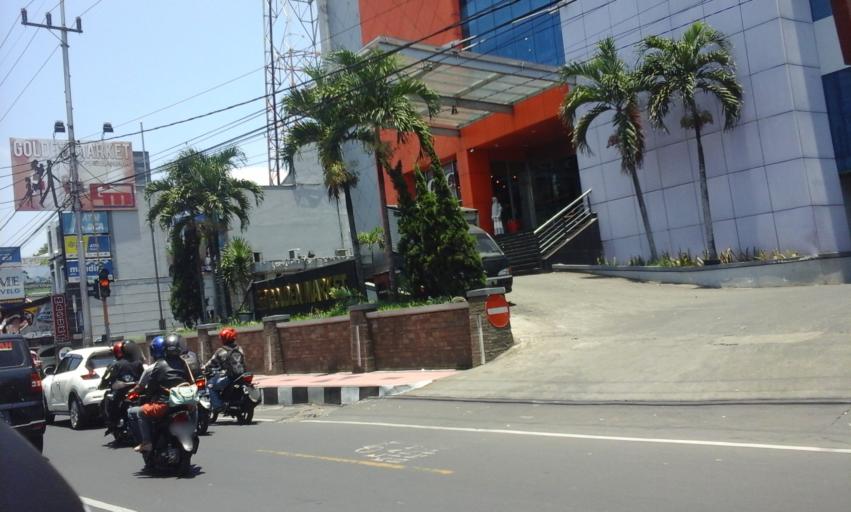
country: ID
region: East Java
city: Kepatihan
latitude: -8.1753
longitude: 113.7021
